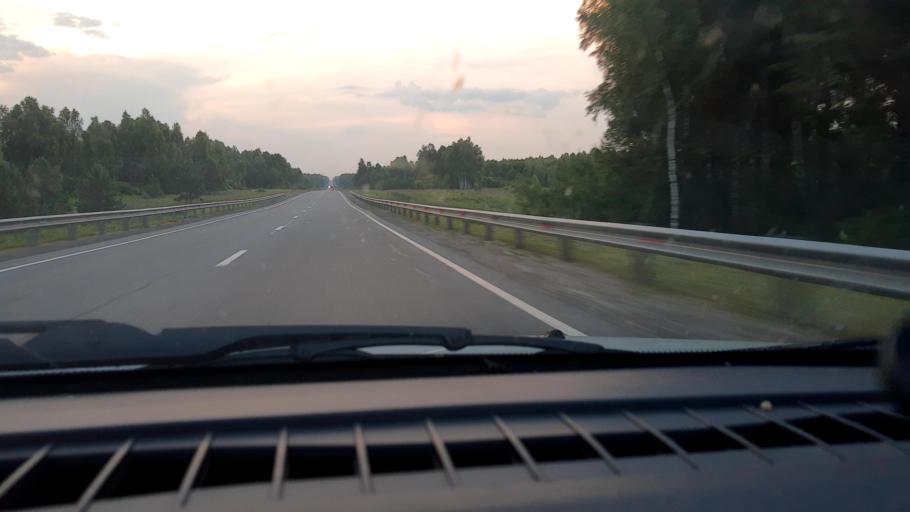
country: RU
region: Nizjnij Novgorod
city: Arzamas
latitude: 55.5434
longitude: 43.9351
